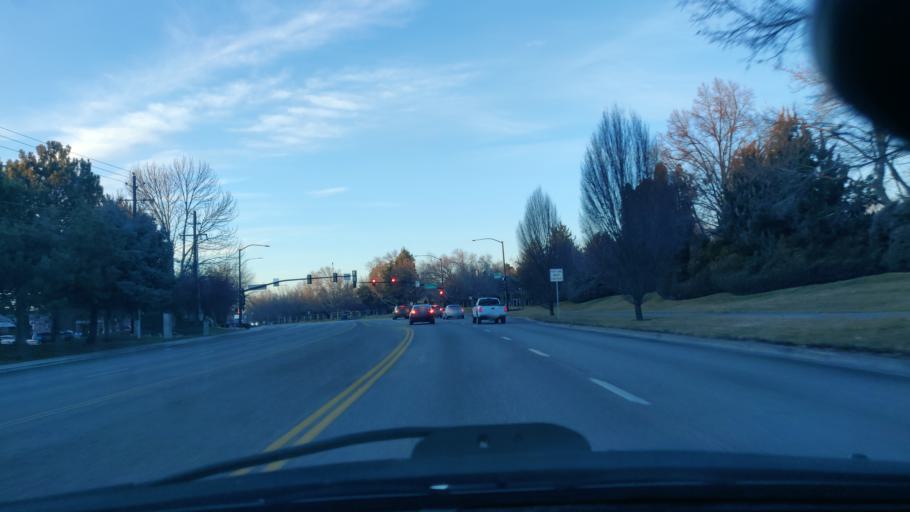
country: US
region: Idaho
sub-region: Ada County
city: Boise
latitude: 43.5885
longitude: -116.1737
